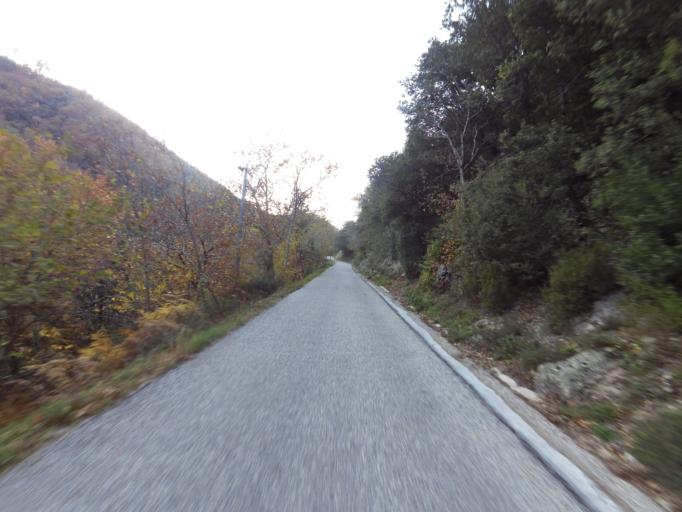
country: FR
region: Rhone-Alpes
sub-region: Departement de l'Ardeche
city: Lablachere
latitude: 44.5195
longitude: 4.1857
